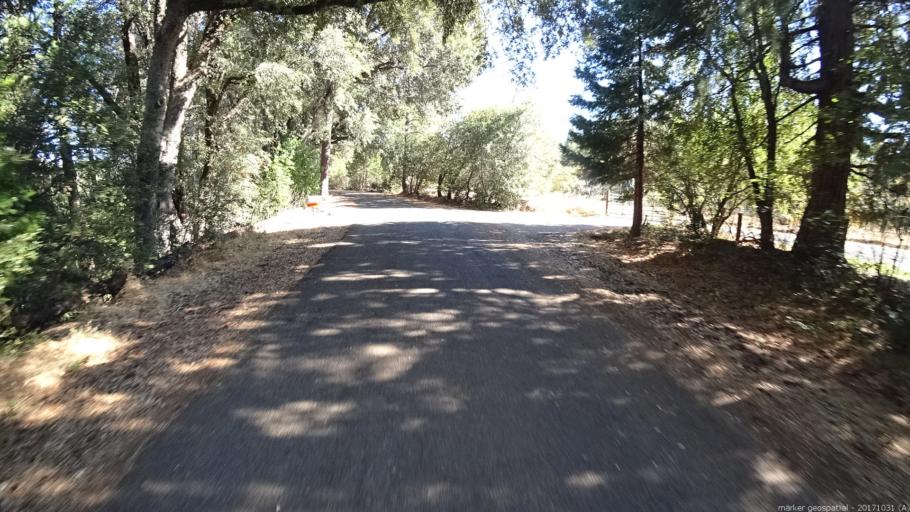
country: US
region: California
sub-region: Shasta County
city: Shingletown
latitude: 40.5305
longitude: -121.9495
